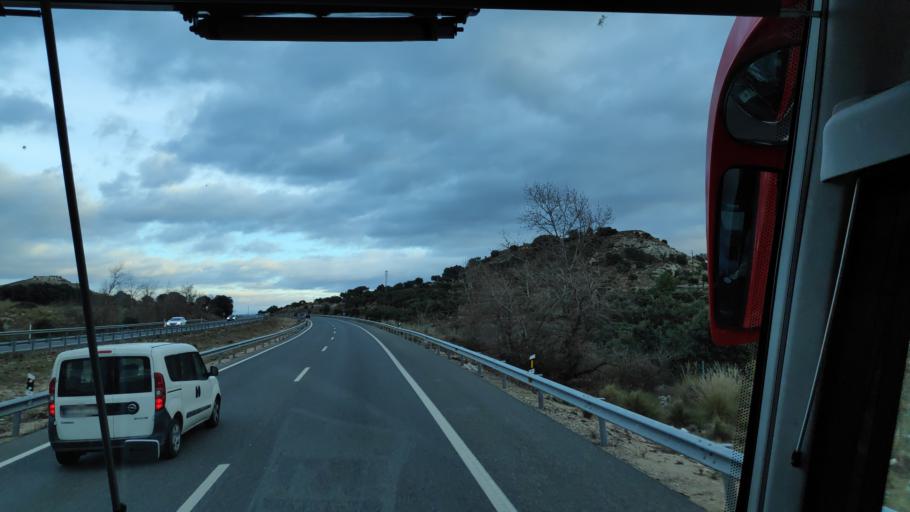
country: ES
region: Madrid
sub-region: Provincia de Madrid
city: Fuentiduena de Tajo
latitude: 40.1414
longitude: -3.2076
